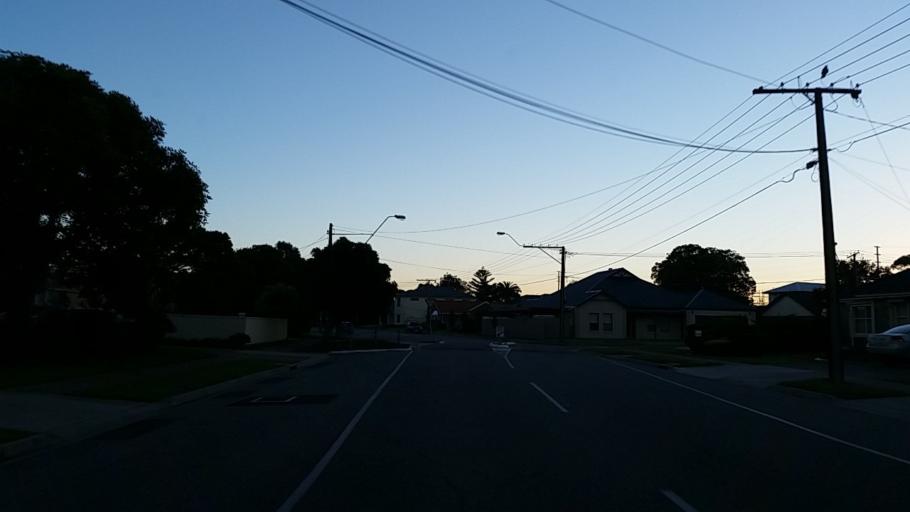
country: AU
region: South Australia
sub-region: Charles Sturt
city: Henley Beach
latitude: -34.9228
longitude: 138.5045
